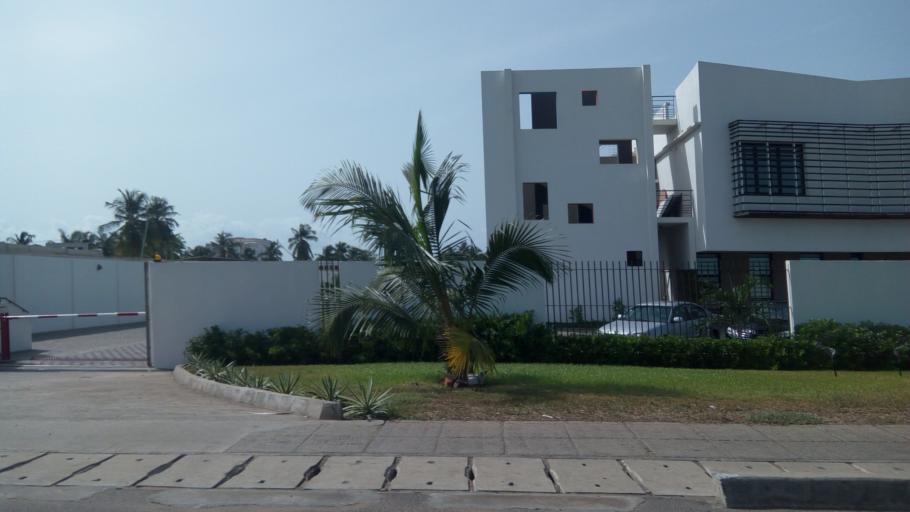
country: TG
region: Maritime
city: Lome
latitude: 6.1301
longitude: 1.2443
